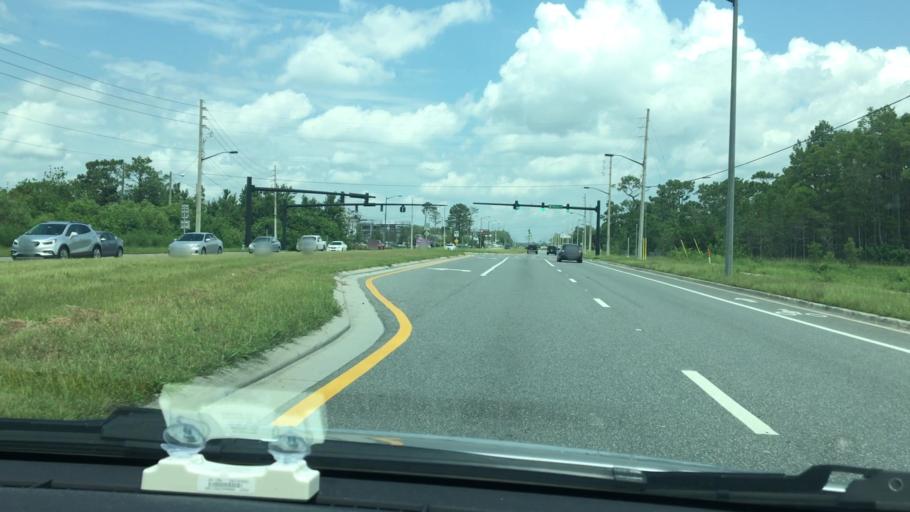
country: US
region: Florida
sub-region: Orange County
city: Conway
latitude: 28.4509
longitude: -81.2658
